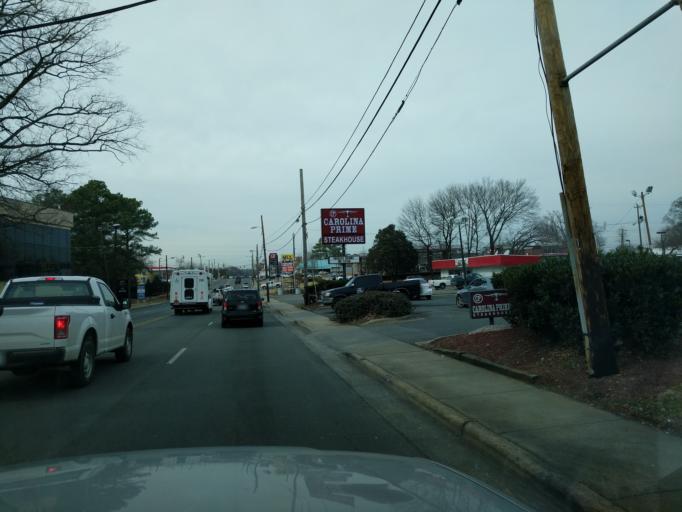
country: US
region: North Carolina
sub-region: Mecklenburg County
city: Charlotte
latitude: 35.1784
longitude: -80.8808
